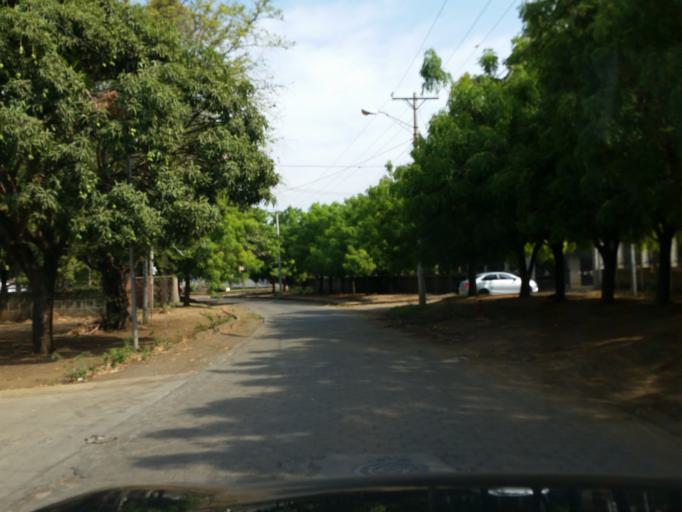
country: NI
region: Managua
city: Managua
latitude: 12.0940
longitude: -86.2245
